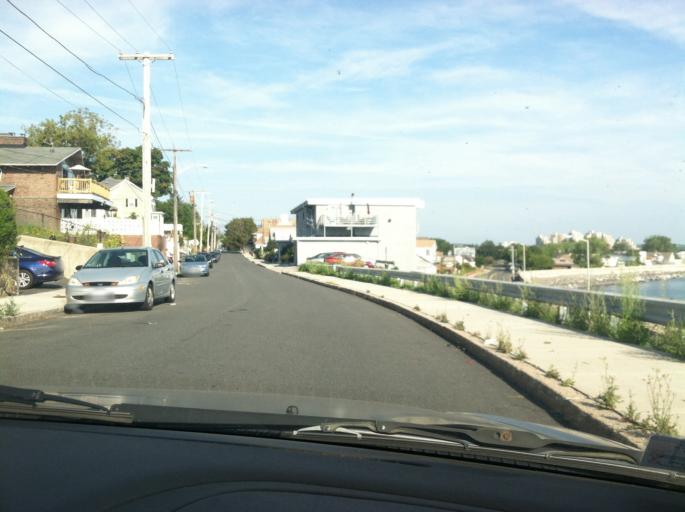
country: US
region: Massachusetts
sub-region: Suffolk County
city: Winthrop
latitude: 42.3954
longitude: -70.9829
